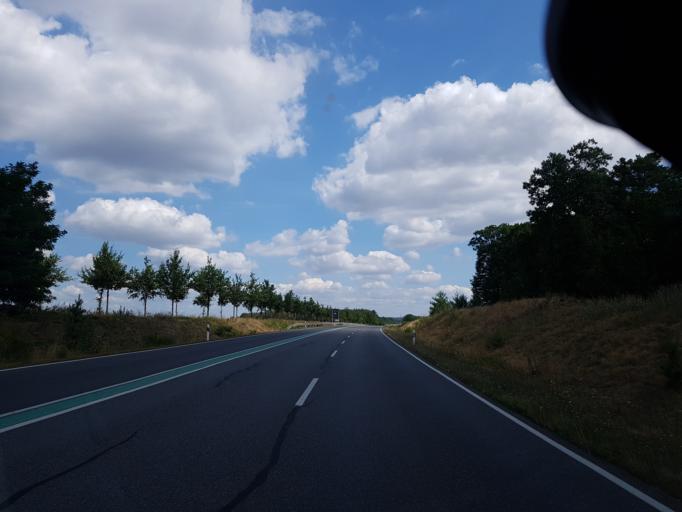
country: DE
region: Brandenburg
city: Drebkau
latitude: 51.6661
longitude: 14.2425
